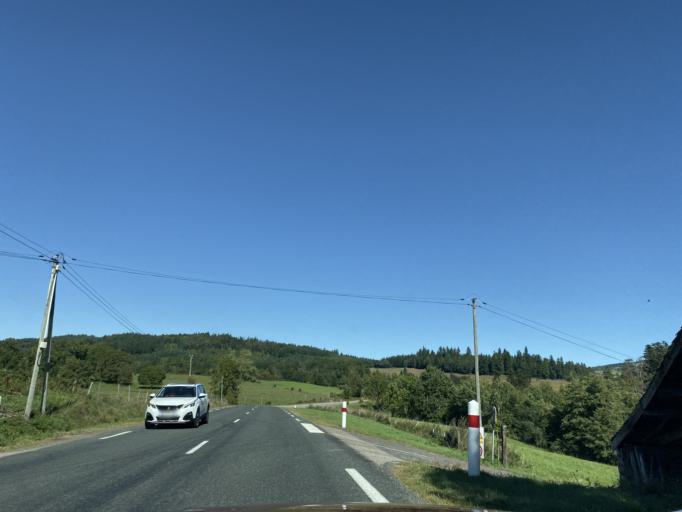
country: FR
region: Rhone-Alpes
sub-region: Departement de la Loire
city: Saint-Just-en-Chevalet
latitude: 45.8881
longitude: 3.8440
